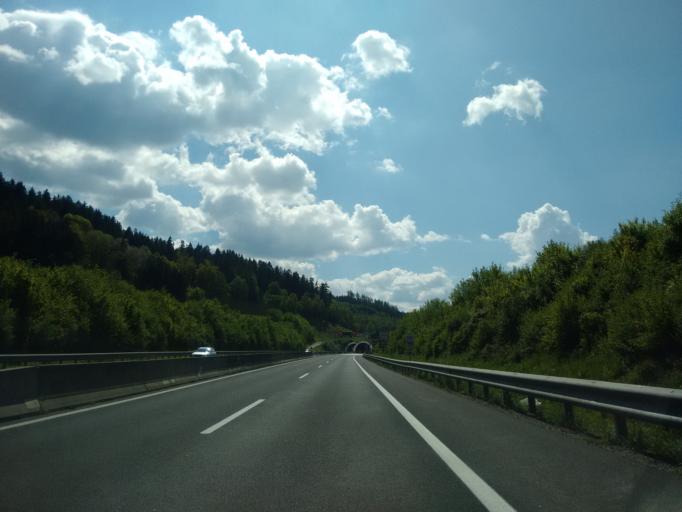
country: AT
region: Styria
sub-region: Politischer Bezirk Leoben
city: Niklasdorf
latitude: 47.3969
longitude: 15.1691
